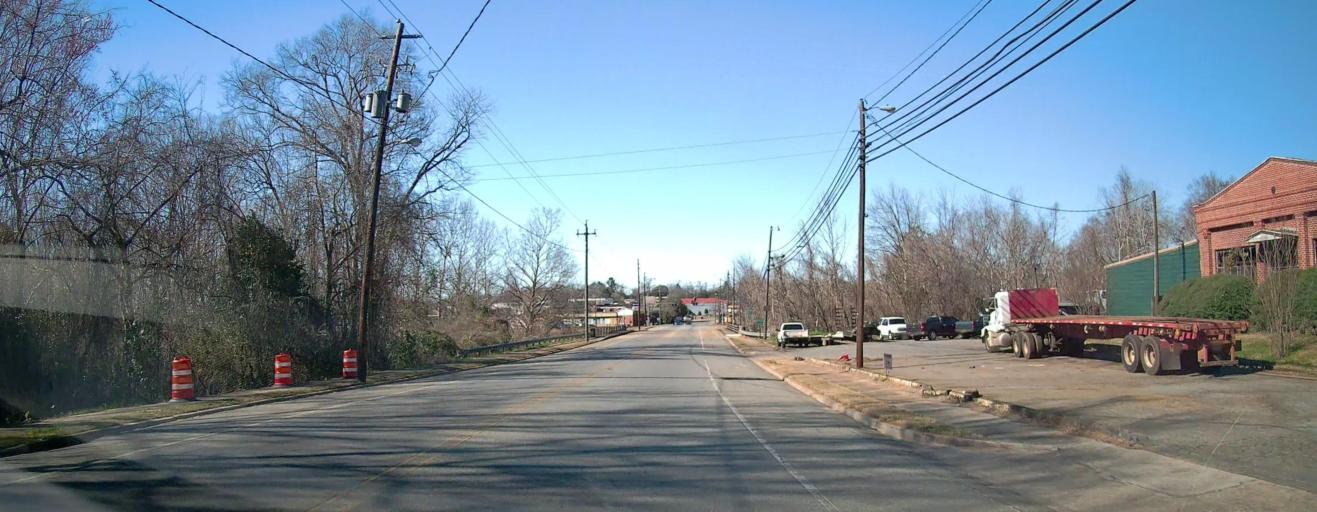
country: US
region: Georgia
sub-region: Macon County
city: Montezuma
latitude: 32.2972
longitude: -84.0266
